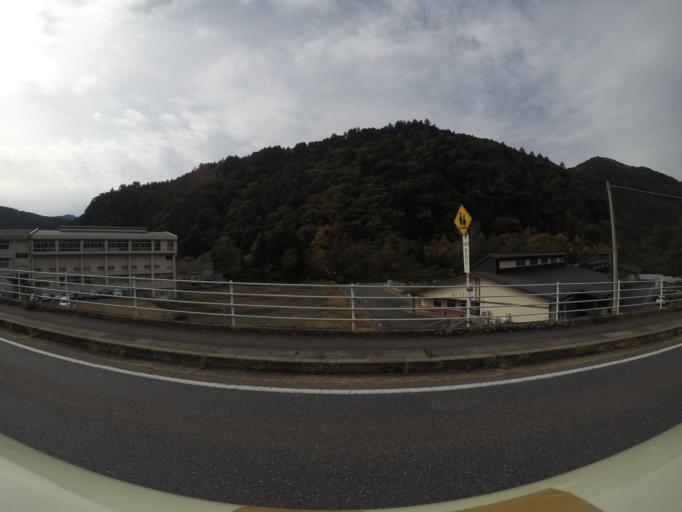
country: JP
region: Nagano
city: Ina
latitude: 35.8587
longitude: 137.7045
